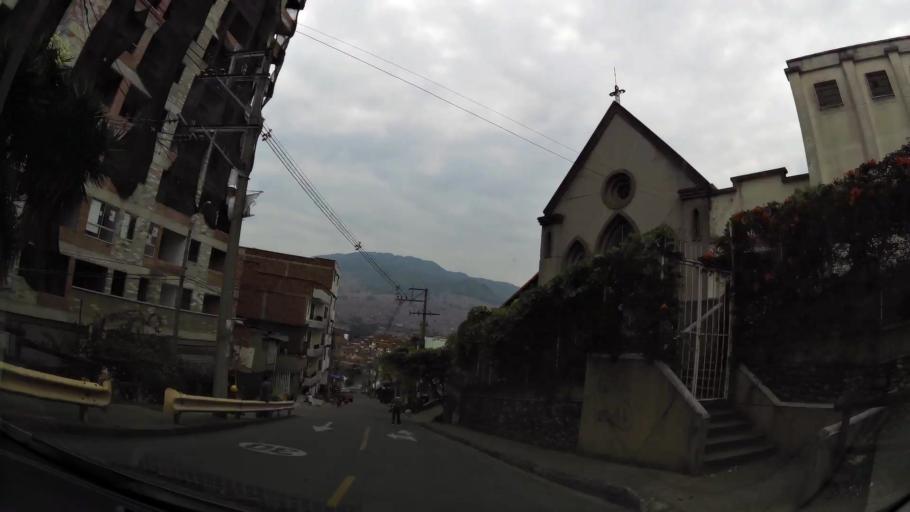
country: CO
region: Antioquia
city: Medellin
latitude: 6.2765
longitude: -75.5620
